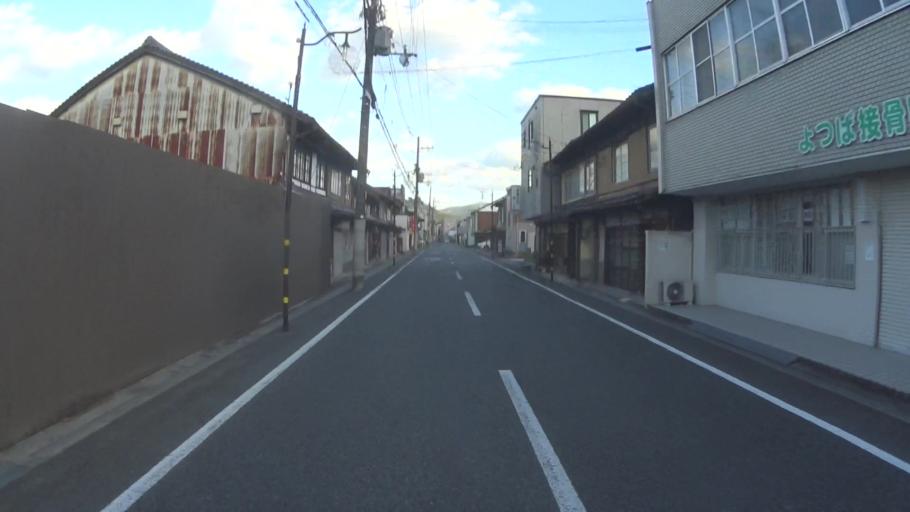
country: JP
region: Kyoto
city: Ayabe
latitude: 35.2985
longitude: 135.2532
